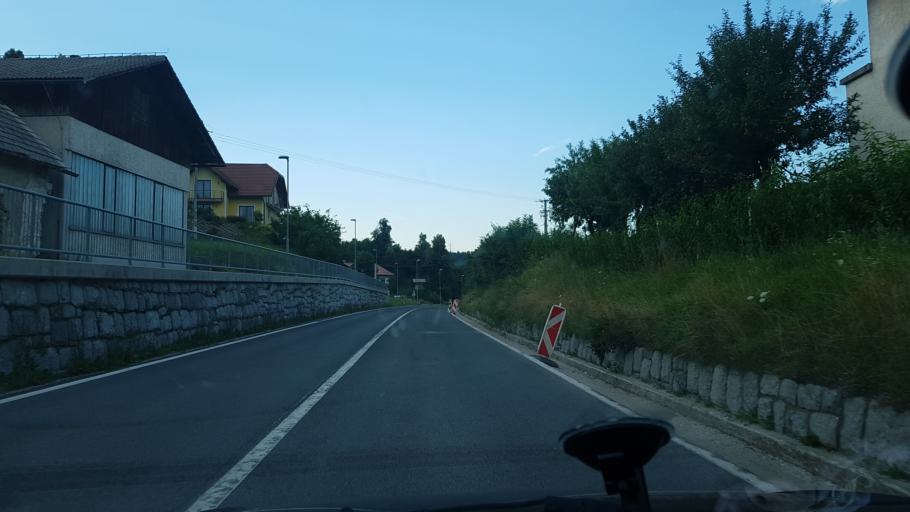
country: SI
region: Logatec
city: Logatec
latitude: 45.9007
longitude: 14.2009
